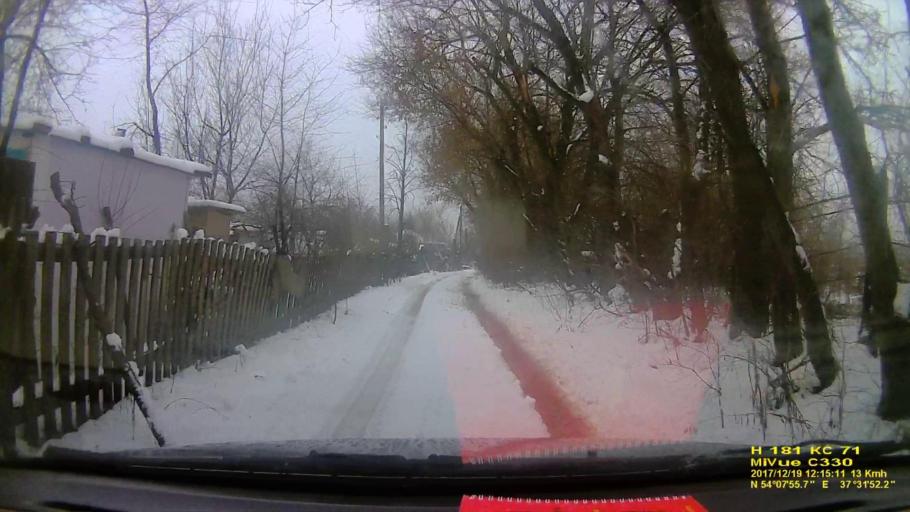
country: RU
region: Tula
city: Kosaya Gora
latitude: 54.1321
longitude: 37.5312
